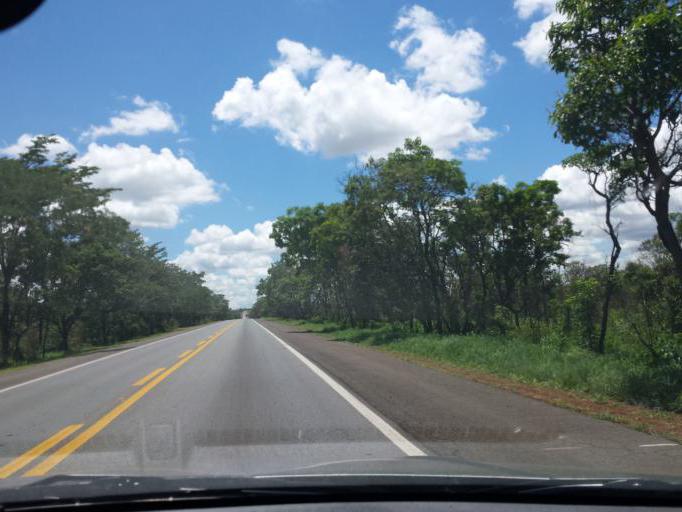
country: BR
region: Goias
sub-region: Cristalina
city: Cristalina
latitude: -16.6556
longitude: -47.7304
